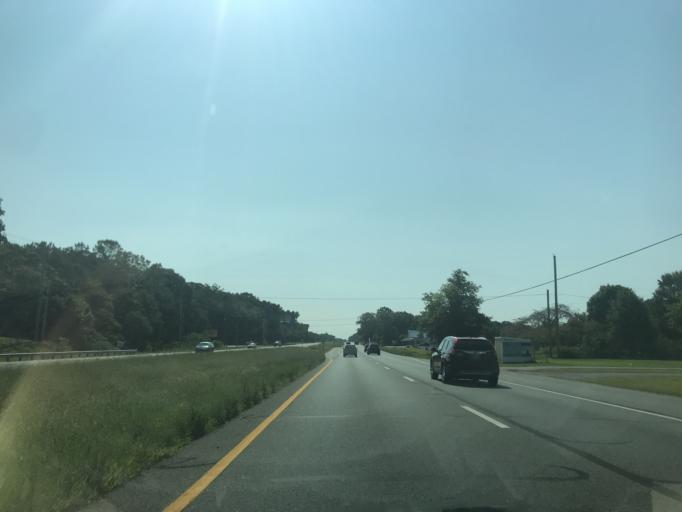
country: US
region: Maryland
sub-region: Saint Mary's County
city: Mechanicsville
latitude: 38.4595
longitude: -76.7617
